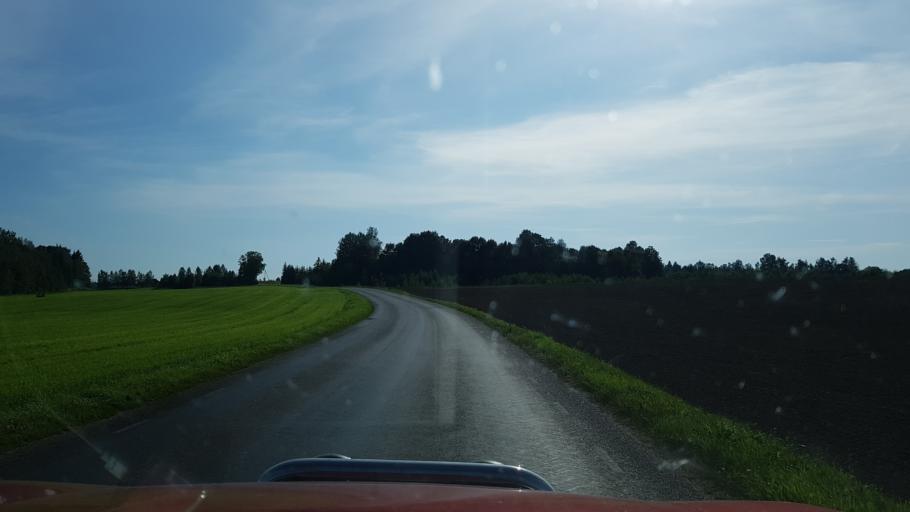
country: EE
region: Viljandimaa
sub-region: Viiratsi vald
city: Viiratsi
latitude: 58.2645
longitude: 25.6194
